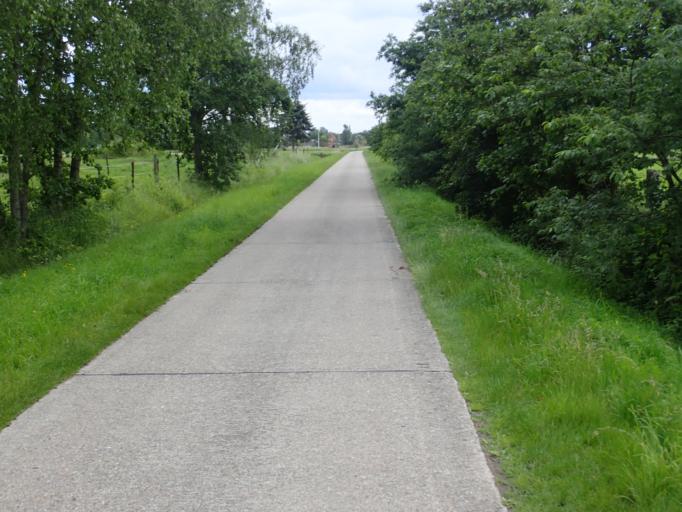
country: BE
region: Flanders
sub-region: Provincie Antwerpen
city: Heist-op-den-Berg
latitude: 51.1115
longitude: 4.7152
